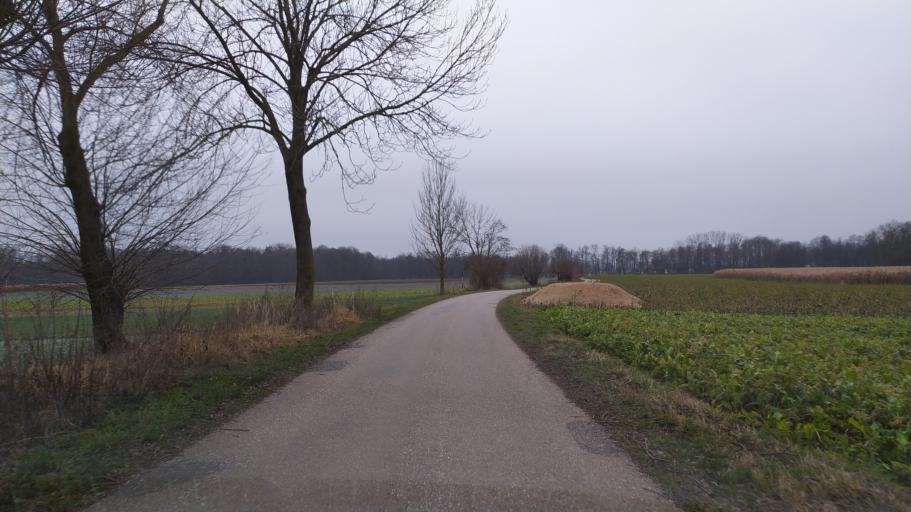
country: AT
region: Upper Austria
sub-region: Politischer Bezirk Perg
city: Perg
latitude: 48.2169
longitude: 14.7203
